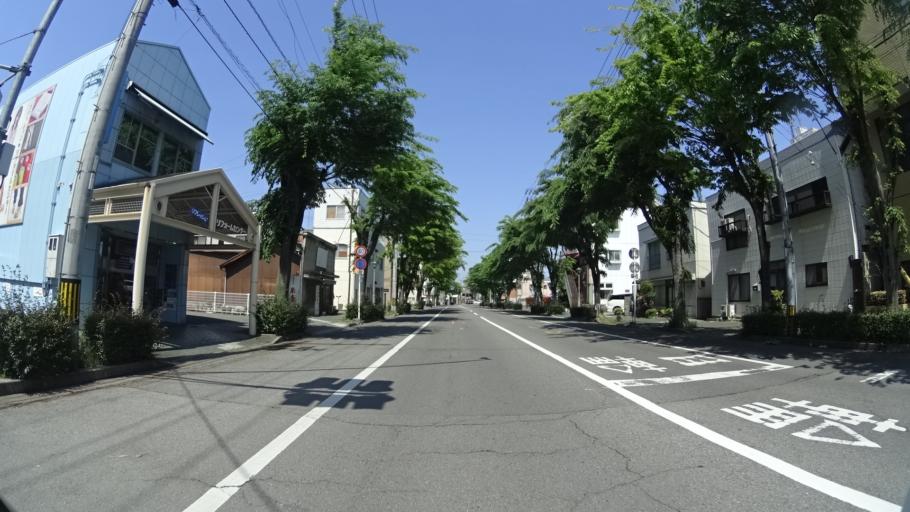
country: JP
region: Ehime
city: Saijo
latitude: 34.0587
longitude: 133.0015
